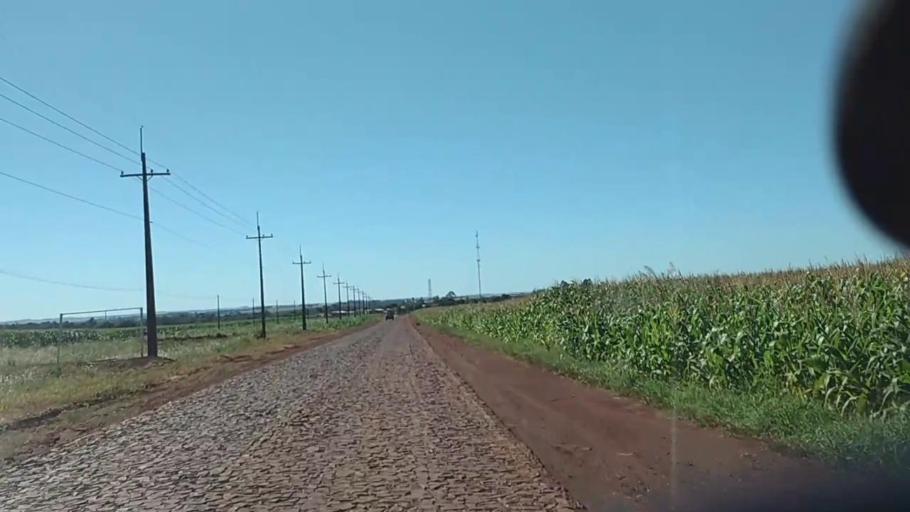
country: PY
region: Alto Parana
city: Naranjal
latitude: -25.9738
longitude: -55.2090
